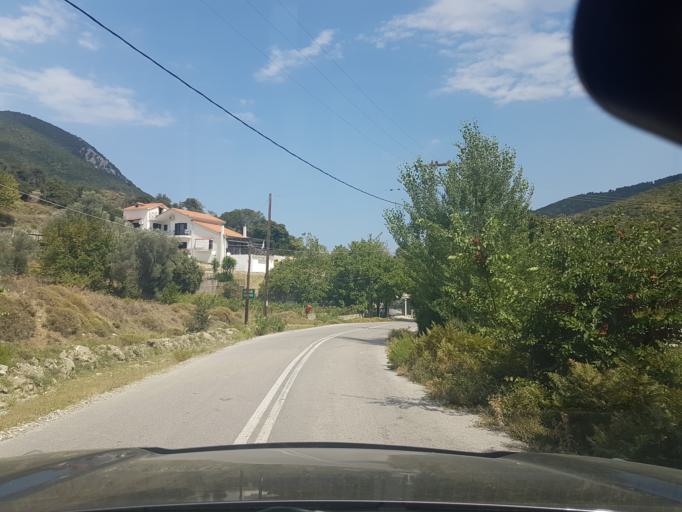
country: GR
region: Central Greece
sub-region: Nomos Evvoias
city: Kymi
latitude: 38.6353
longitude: 24.0743
